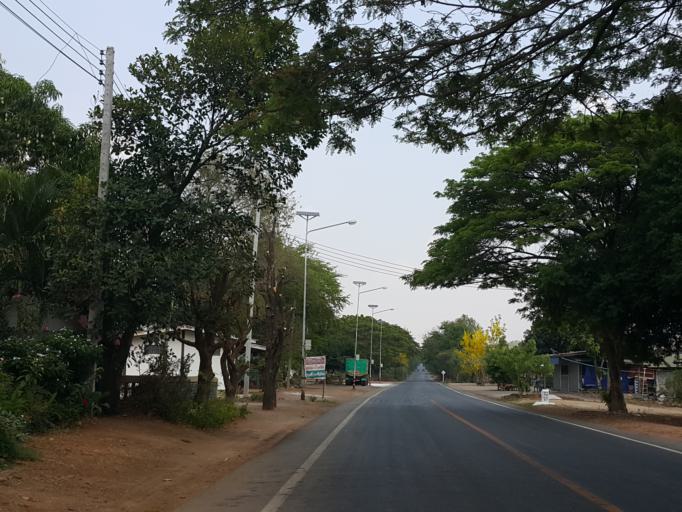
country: TH
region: Kanchanaburi
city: Nong Prue
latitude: 14.5416
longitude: 99.5790
